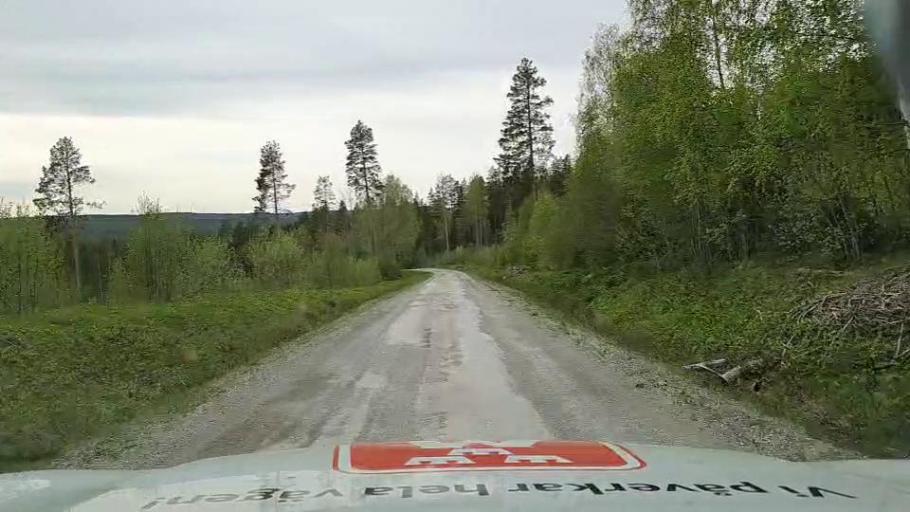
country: SE
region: Jaemtland
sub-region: Bergs Kommun
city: Hoverberg
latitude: 62.6787
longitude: 14.7551
